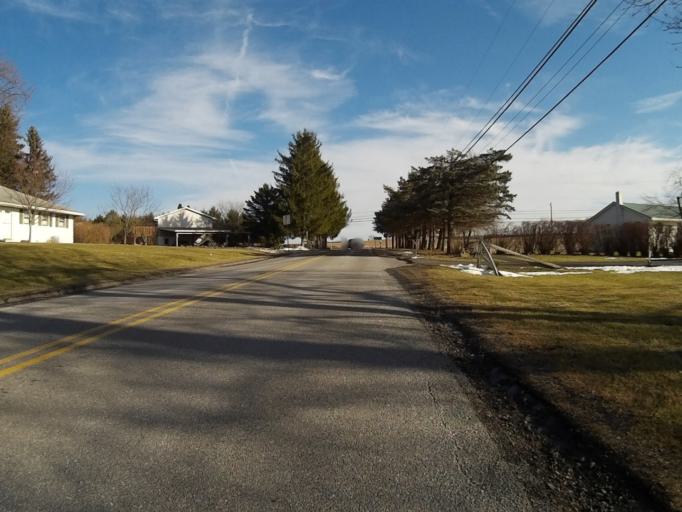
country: US
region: Pennsylvania
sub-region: Centre County
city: Houserville
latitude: 40.8728
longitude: -77.8517
